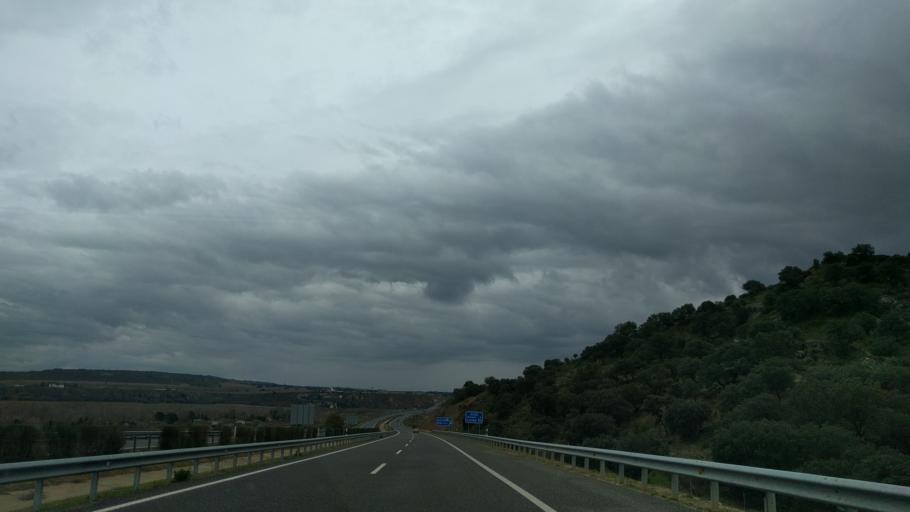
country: ES
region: Aragon
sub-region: Provincia de Huesca
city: Castejon del Puente
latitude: 41.9649
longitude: 0.1615
